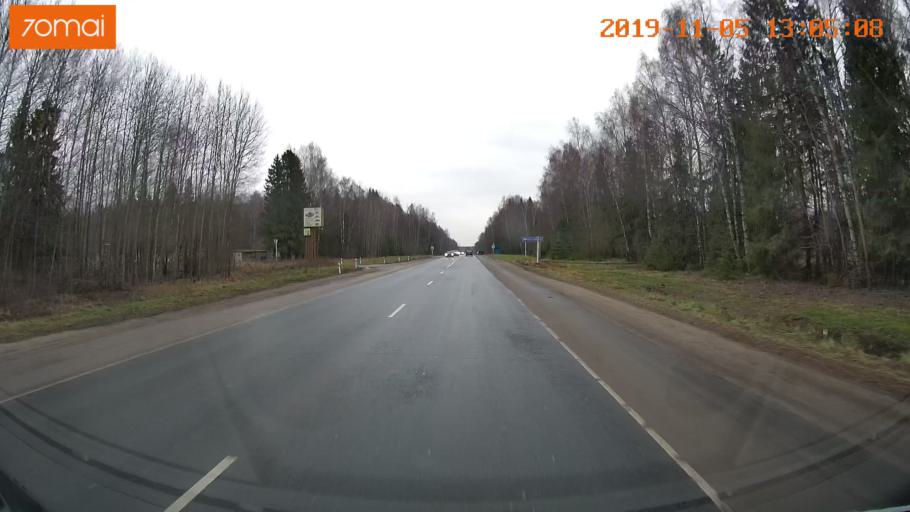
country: RU
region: Ivanovo
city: Kitovo
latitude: 56.8845
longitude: 41.2364
